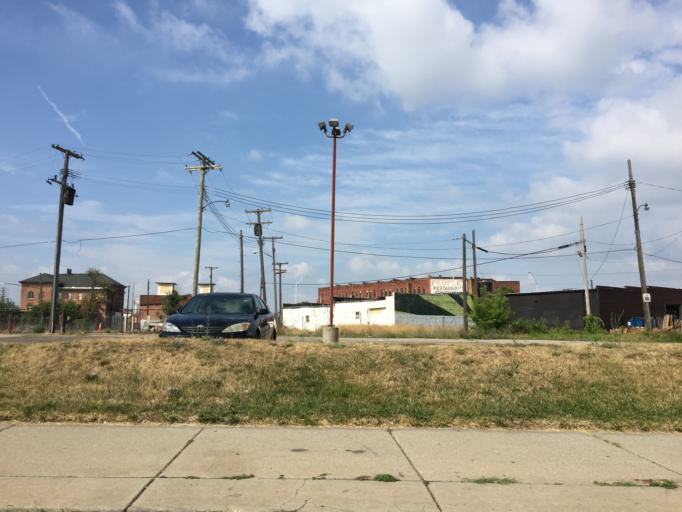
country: US
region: Michigan
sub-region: Wayne County
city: Detroit
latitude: 42.3517
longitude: -83.0315
